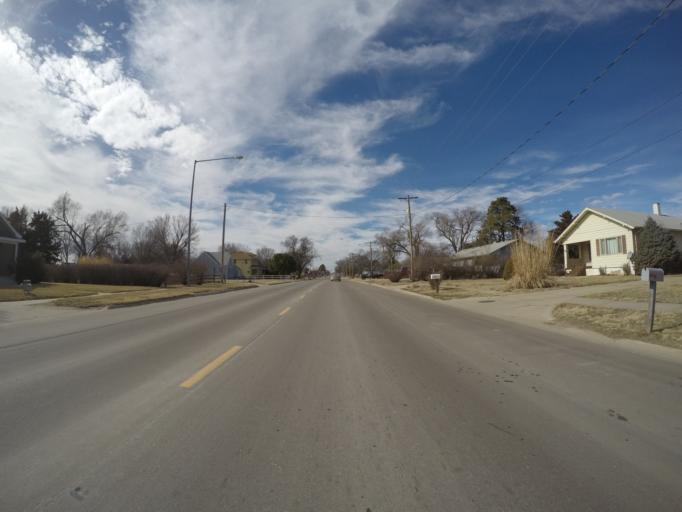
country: US
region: Nebraska
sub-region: Franklin County
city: Franklin
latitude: 40.0961
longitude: -98.9489
